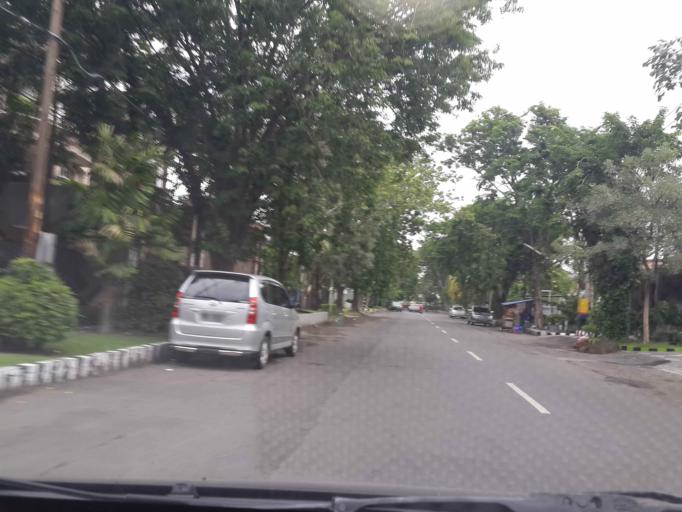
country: ID
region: East Java
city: Gubengairlangga
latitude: -7.2817
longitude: 112.7359
